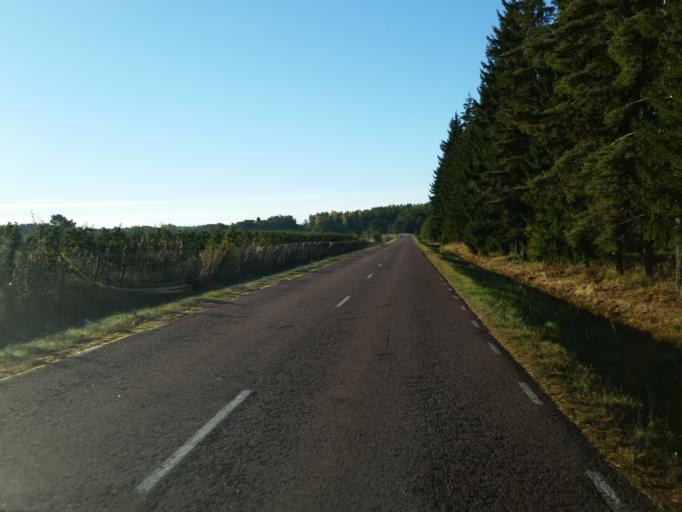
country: AX
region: Alands skaergard
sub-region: Vardoe
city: Vardoe
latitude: 60.2408
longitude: 20.3735
